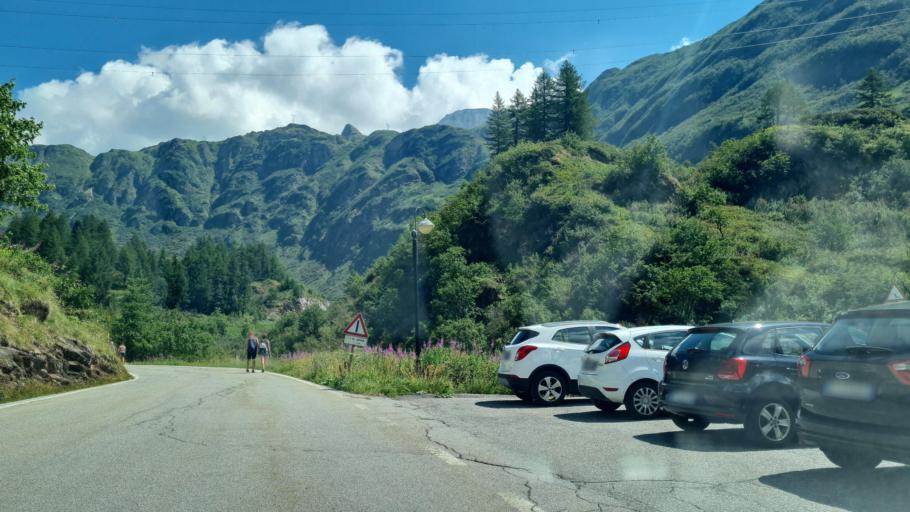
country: IT
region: Piedmont
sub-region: Provincia Verbano-Cusio-Ossola
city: Formazza
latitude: 46.4144
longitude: 8.4108
